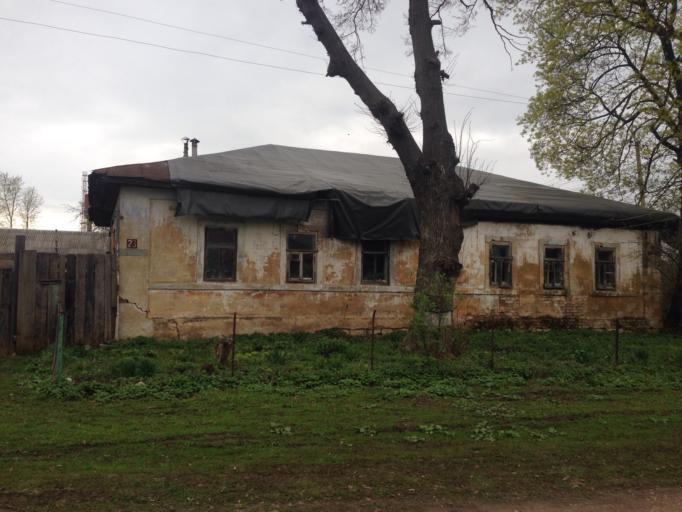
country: RU
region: Tula
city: Krapivna
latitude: 53.9395
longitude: 37.1500
